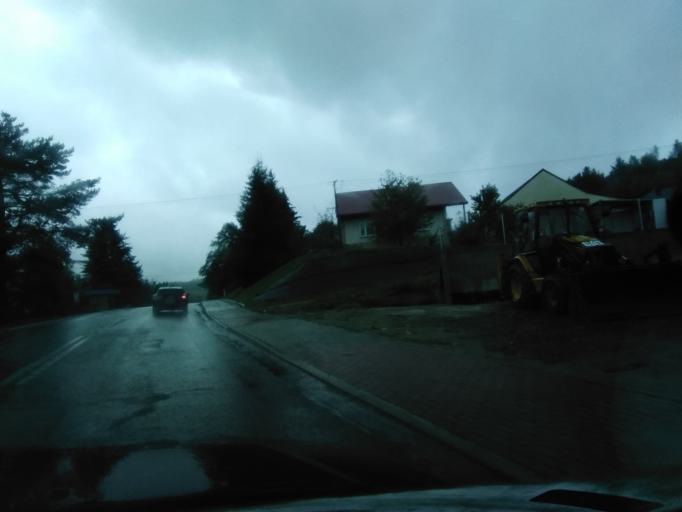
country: PL
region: Subcarpathian Voivodeship
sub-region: Powiat ropczycko-sedziszowski
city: Niedzwiada
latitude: 50.0193
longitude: 21.5474
